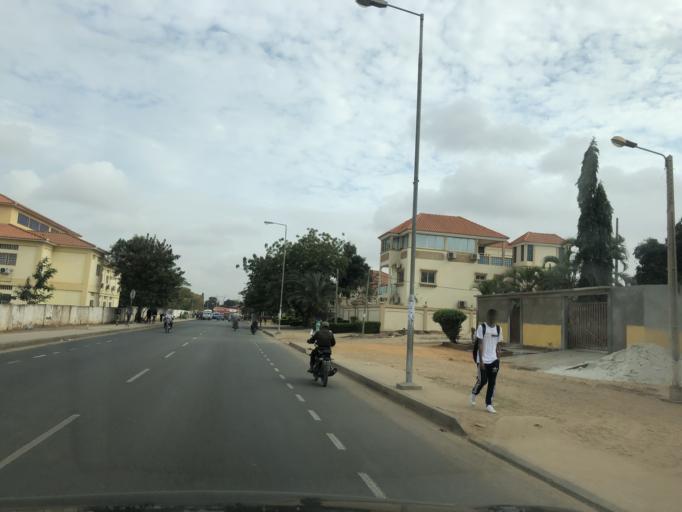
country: AO
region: Luanda
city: Luanda
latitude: -8.9147
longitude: 13.3722
